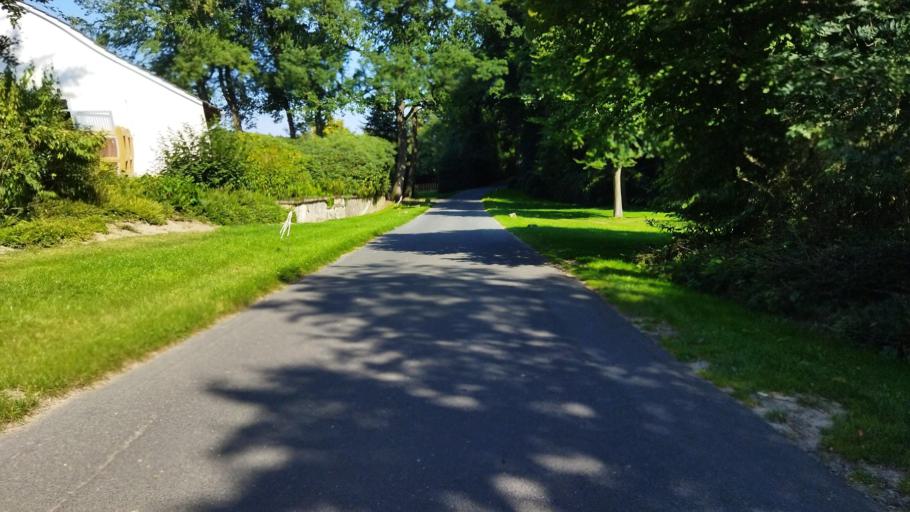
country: DE
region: North Rhine-Westphalia
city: Lengerich
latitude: 52.2258
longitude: 7.8651
